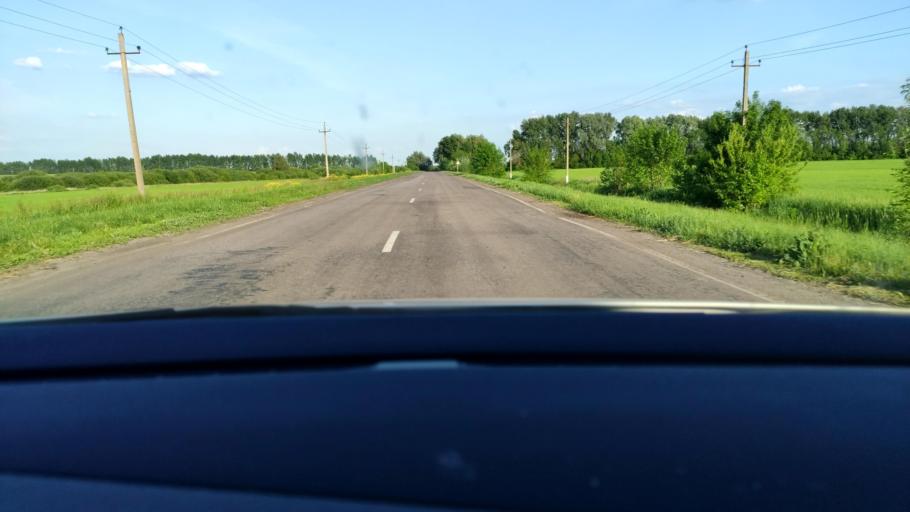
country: RU
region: Voronezj
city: Kashirskoye
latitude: 51.4924
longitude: 39.8450
